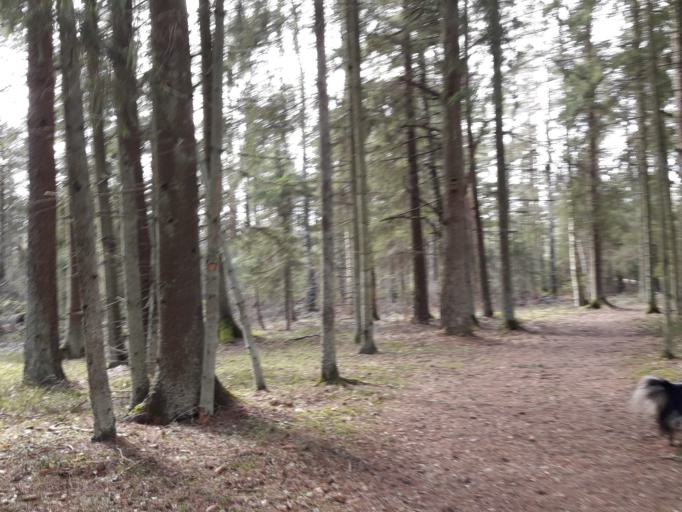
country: LV
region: Talsu Rajons
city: Sabile
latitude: 56.9067
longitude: 22.3977
